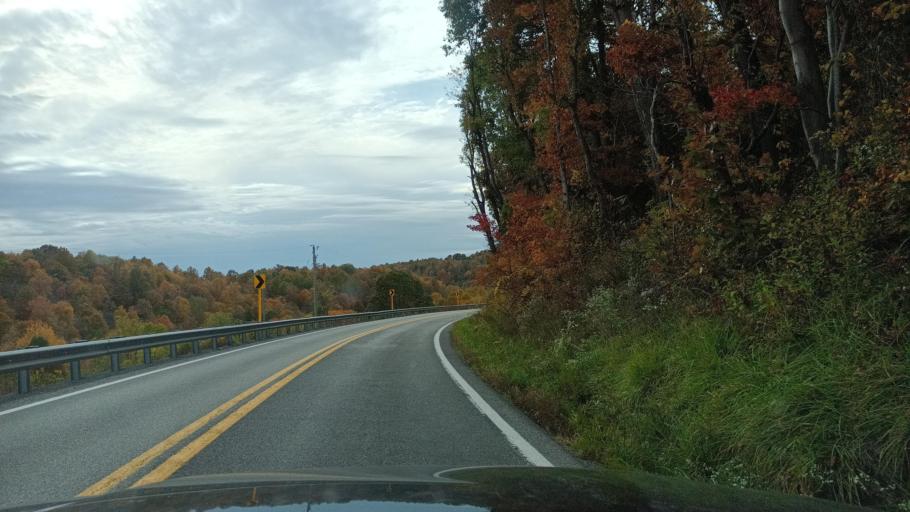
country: US
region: West Virginia
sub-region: Preston County
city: Kingwood
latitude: 39.3319
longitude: -79.7814
